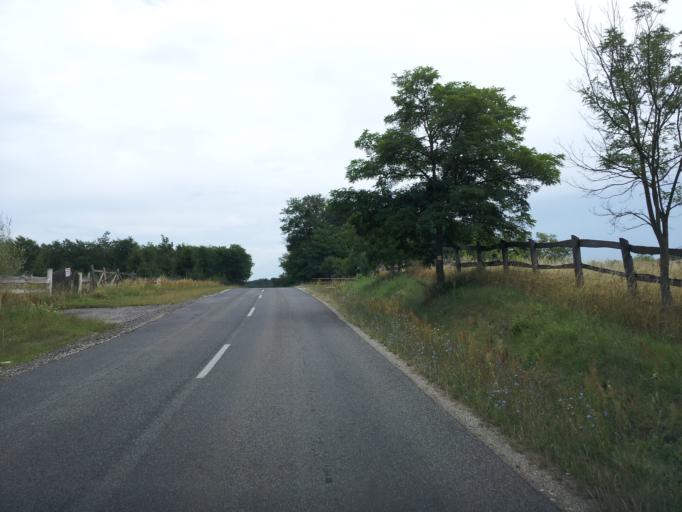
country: HU
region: Vas
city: Vasvar
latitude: 47.0497
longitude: 16.8208
